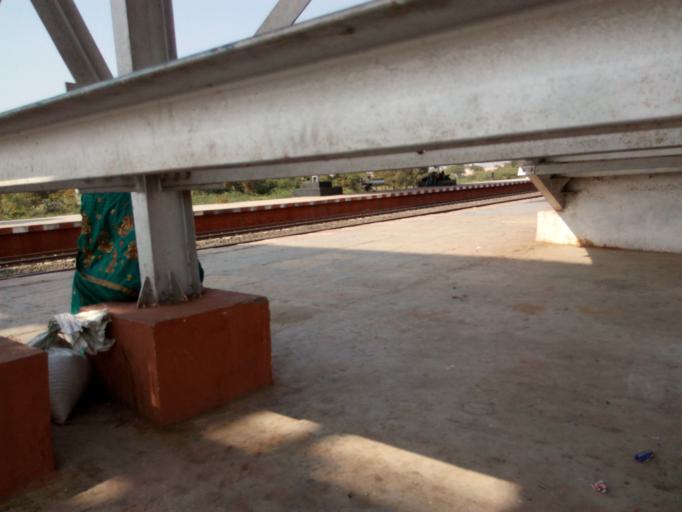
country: IN
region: Maharashtra
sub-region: Solapur
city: Sangola
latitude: 17.4368
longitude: 75.1883
